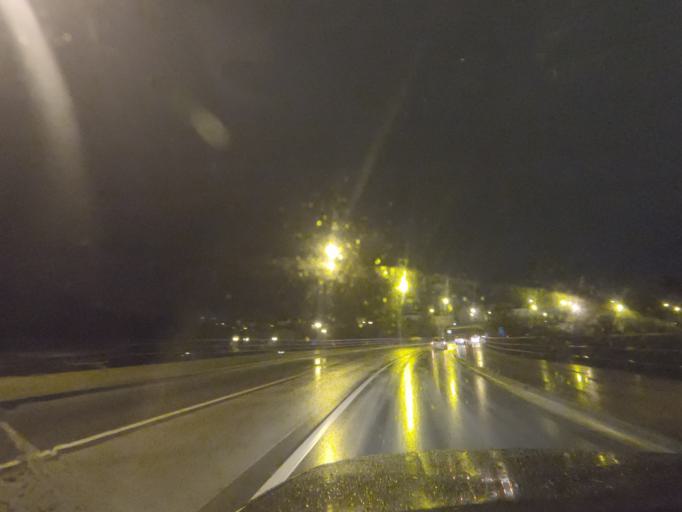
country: PT
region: Vila Real
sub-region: Vila Real
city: Vila Real
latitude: 41.3064
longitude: -7.7348
